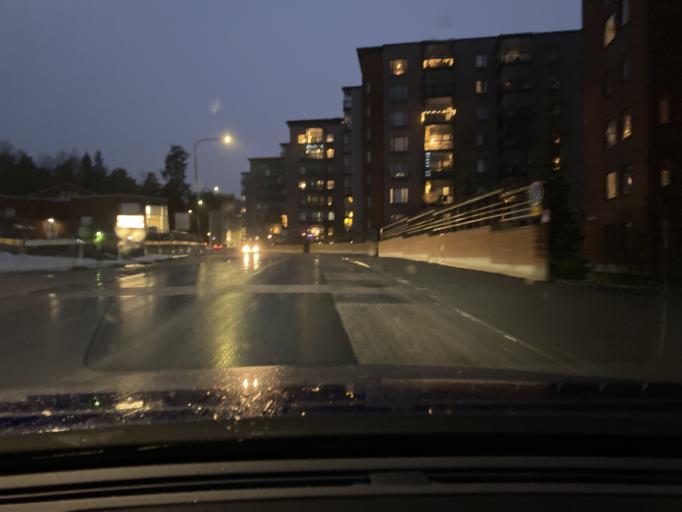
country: FI
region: Pirkanmaa
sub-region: Tampere
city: Tampere
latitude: 61.4950
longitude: 23.8060
